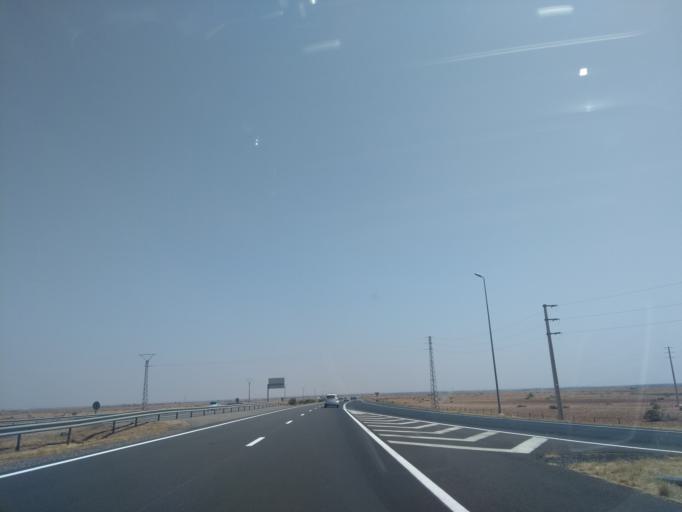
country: MA
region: Marrakech-Tensift-Al Haouz
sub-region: Kelaa-Des-Sraghna
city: Sidi Bou Othmane
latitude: 31.9209
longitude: -8.0237
